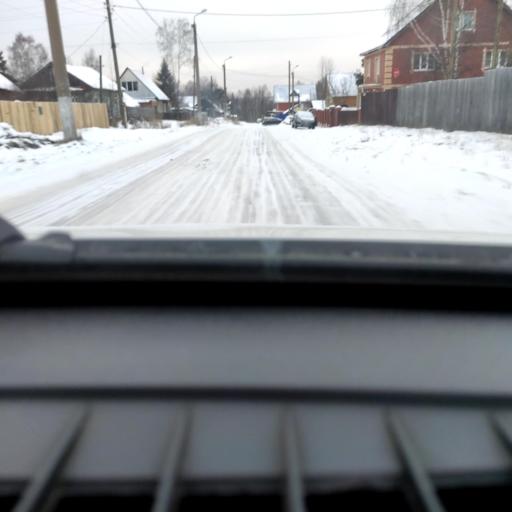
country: RU
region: Perm
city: Perm
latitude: 58.1021
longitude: 56.3675
